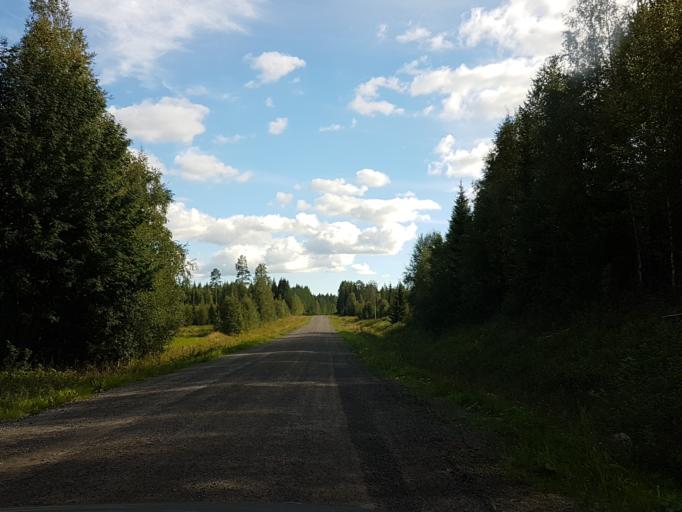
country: SE
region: Vaesterbotten
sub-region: Robertsfors Kommun
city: Robertsfors
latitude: 64.1805
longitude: 20.6446
